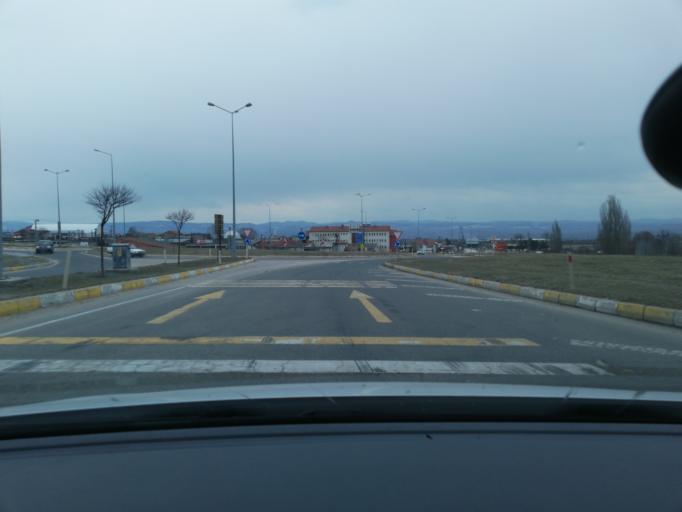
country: TR
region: Bolu
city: Gerede
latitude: 40.7920
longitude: 32.2077
